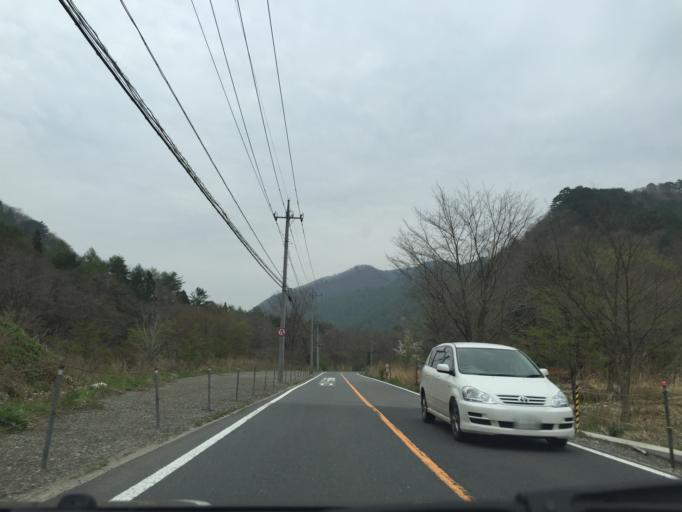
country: JP
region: Tochigi
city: Nikko
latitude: 37.0239
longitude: 139.7269
